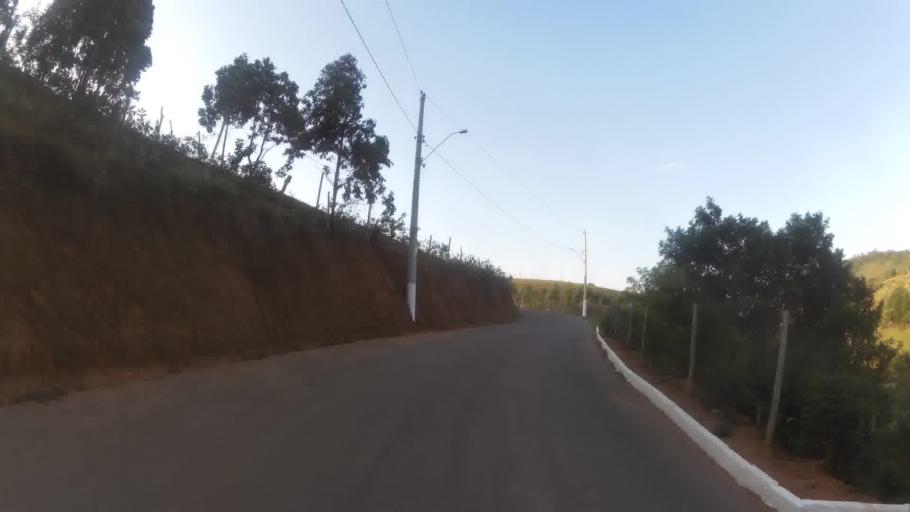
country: BR
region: Espirito Santo
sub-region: Iconha
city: Iconha
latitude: -20.9002
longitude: -40.8109
